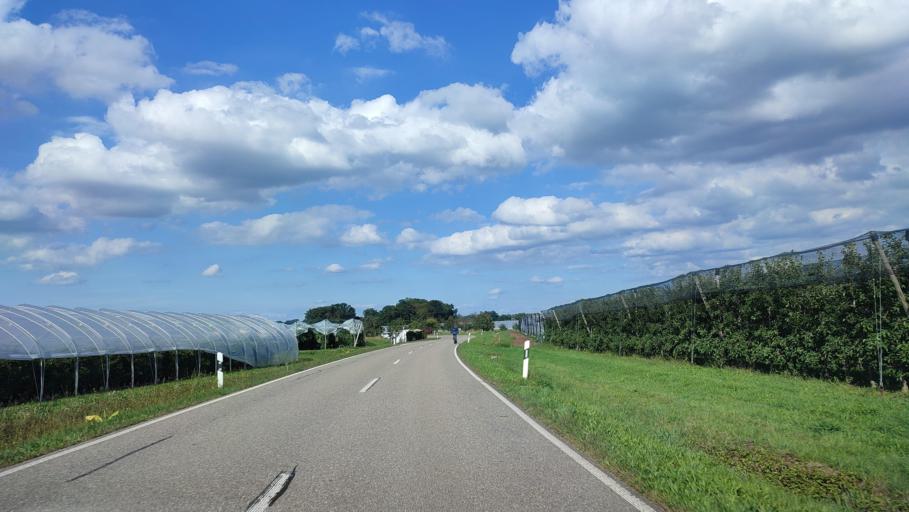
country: DE
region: Baden-Wuerttemberg
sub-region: Freiburg Region
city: Renchen
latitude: 48.5554
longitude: 8.0207
